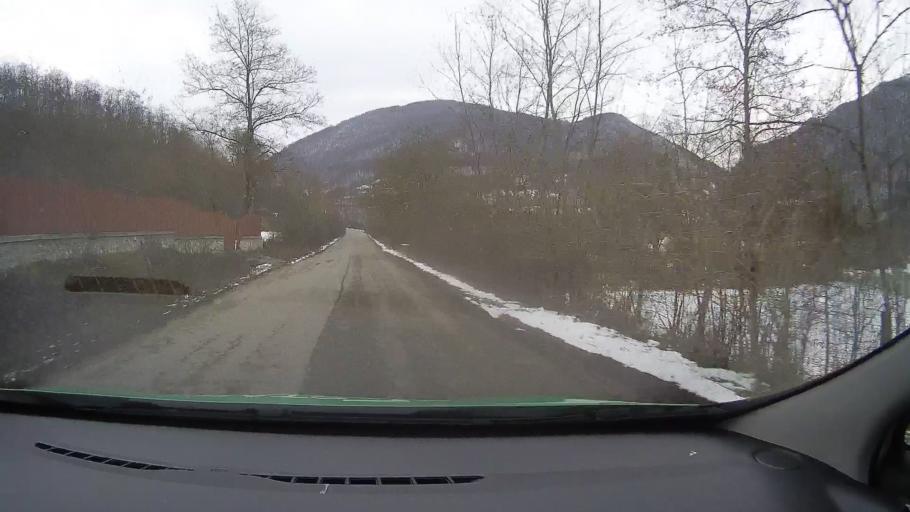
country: RO
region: Hunedoara
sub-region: Comuna Balsa
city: Balsa
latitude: 46.0223
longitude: 23.1213
